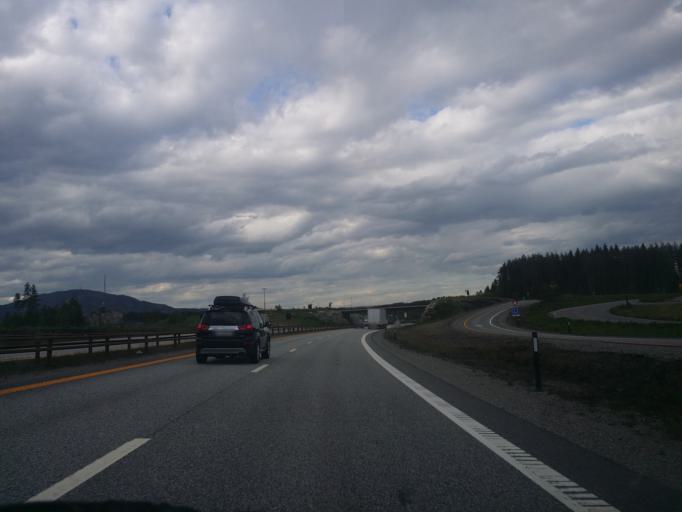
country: NO
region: Akershus
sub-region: Eidsvoll
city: Raholt
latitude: 60.3120
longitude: 11.1431
